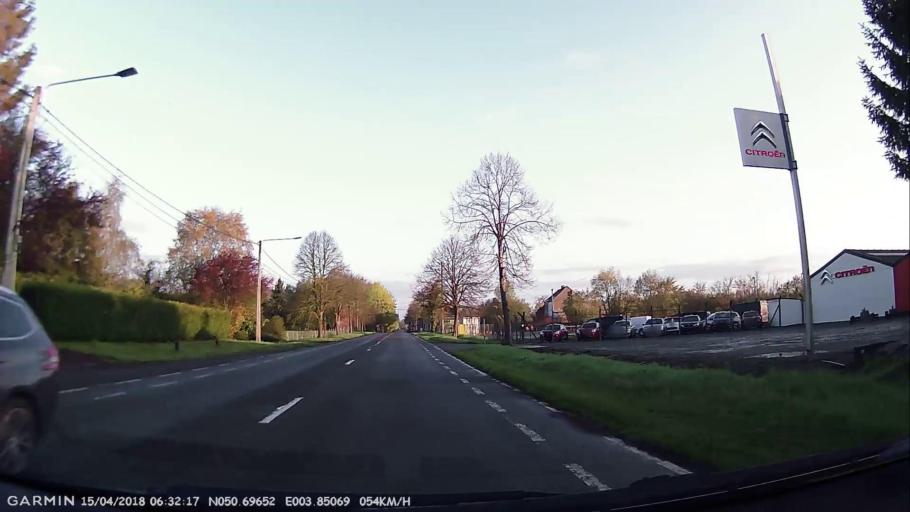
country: BE
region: Wallonia
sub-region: Province du Hainaut
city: Lessines
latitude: 50.6966
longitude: 3.8507
